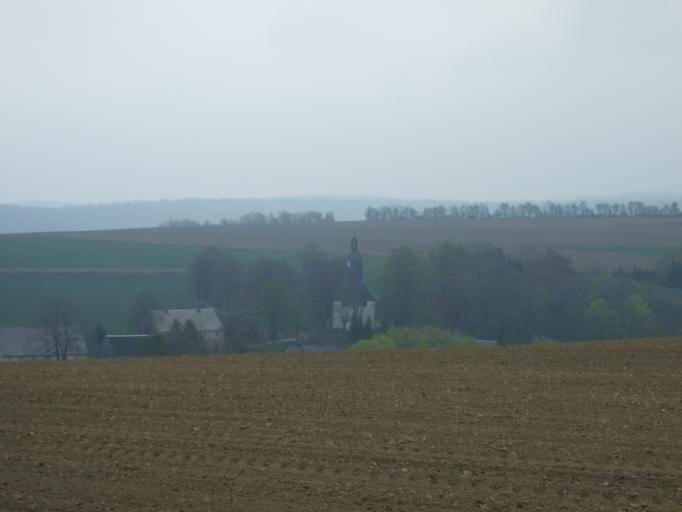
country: DE
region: Saxony
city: Rechenberg-Bienenmuhle
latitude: 50.7605
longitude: 13.5388
